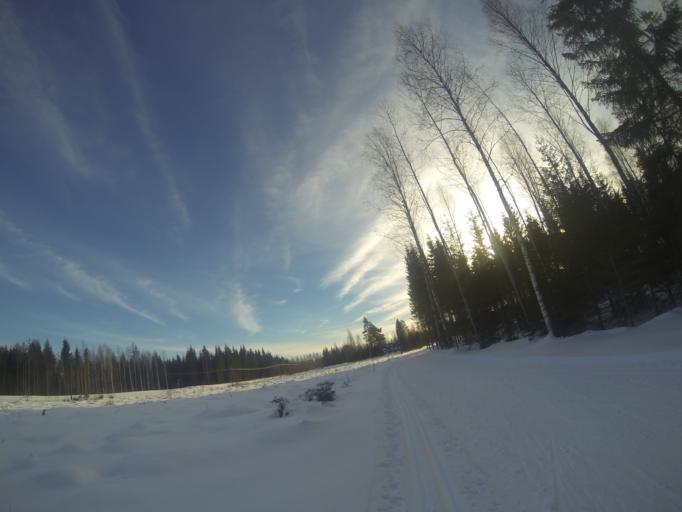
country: FI
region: Southern Savonia
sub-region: Savonlinna
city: Savonlinna
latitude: 61.9458
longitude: 28.9200
